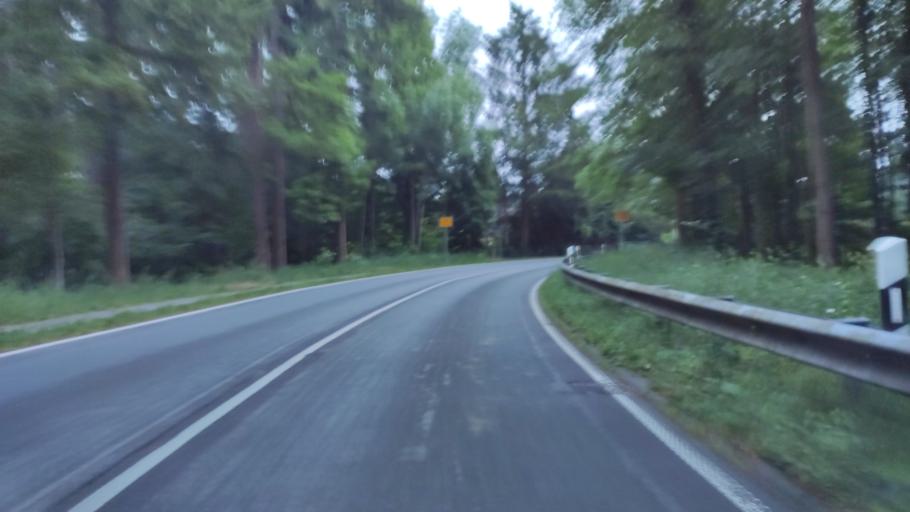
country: DE
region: North Rhine-Westphalia
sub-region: Regierungsbezirk Dusseldorf
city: Dormagen
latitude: 51.1113
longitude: 6.7442
